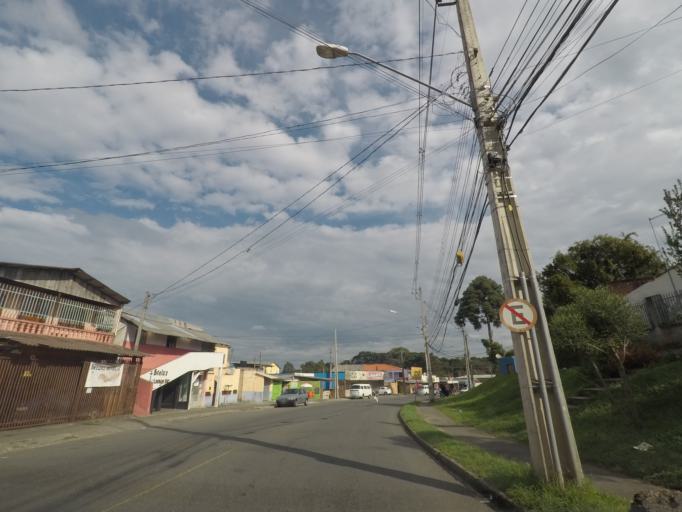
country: BR
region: Parana
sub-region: Sao Jose Dos Pinhais
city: Sao Jose dos Pinhais
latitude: -25.5525
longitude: -49.2926
